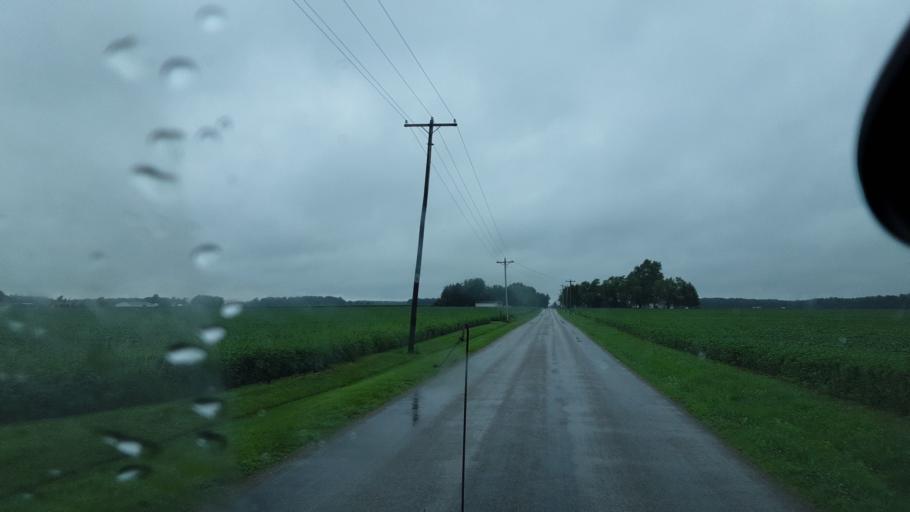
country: US
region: Indiana
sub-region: Adams County
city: Decatur
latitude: 40.7385
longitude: -84.8552
